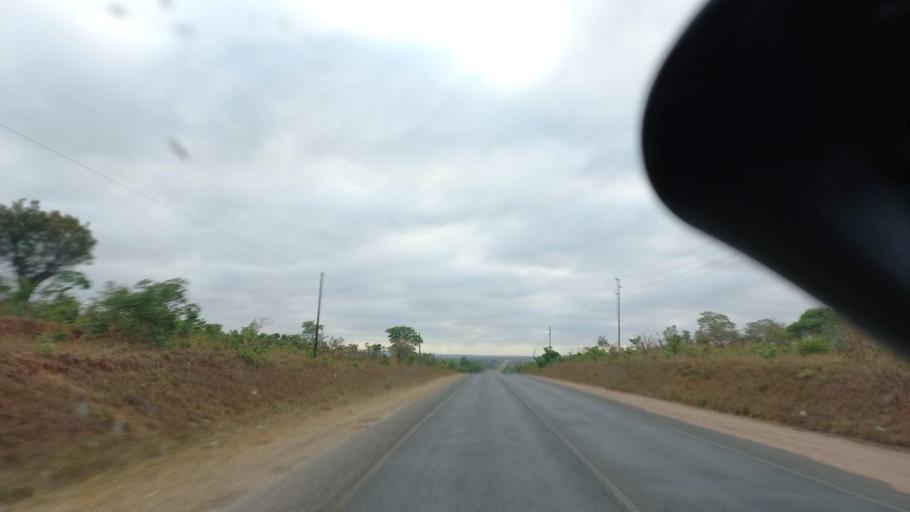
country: ZM
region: Lusaka
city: Chongwe
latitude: -15.3415
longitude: 28.6036
